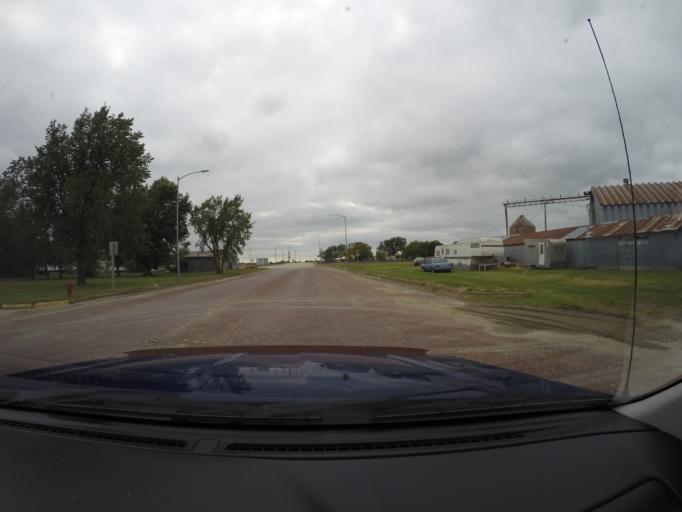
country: US
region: Kansas
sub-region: Dickinson County
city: Herington
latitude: 38.7957
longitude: -96.7397
